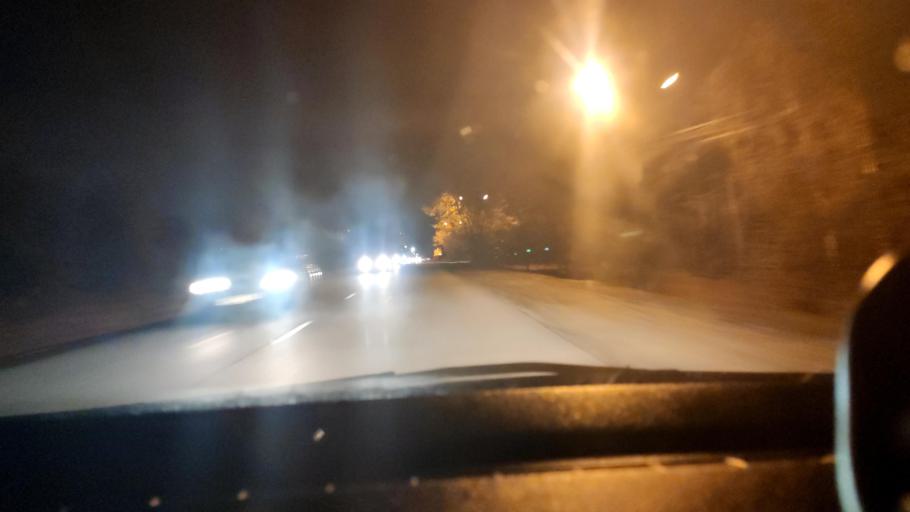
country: RU
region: Voronezj
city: Shilovo
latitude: 51.5582
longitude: 39.1062
